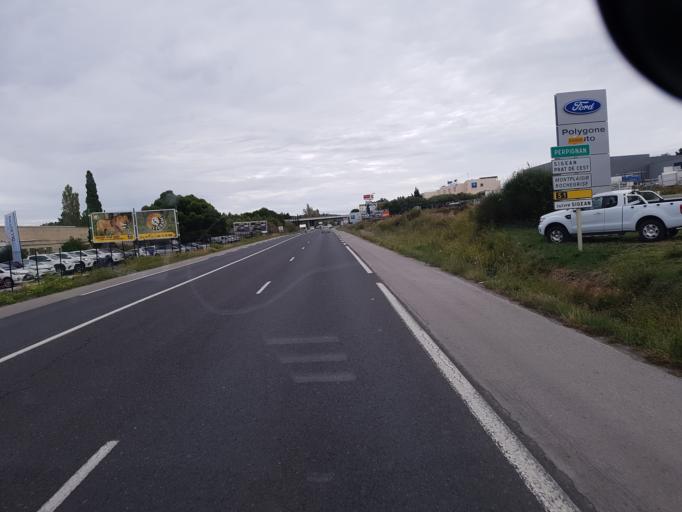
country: FR
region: Languedoc-Roussillon
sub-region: Departement de l'Aude
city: Narbonne
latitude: 43.1547
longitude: 2.9806
